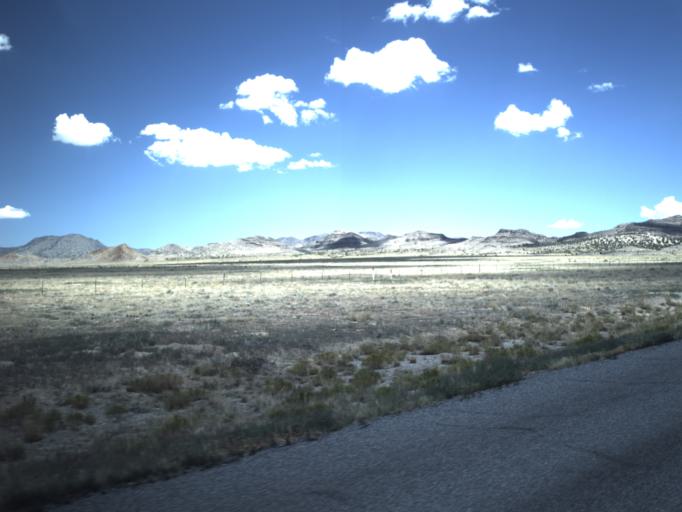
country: US
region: Utah
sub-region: Beaver County
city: Milford
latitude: 39.0636
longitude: -113.7471
